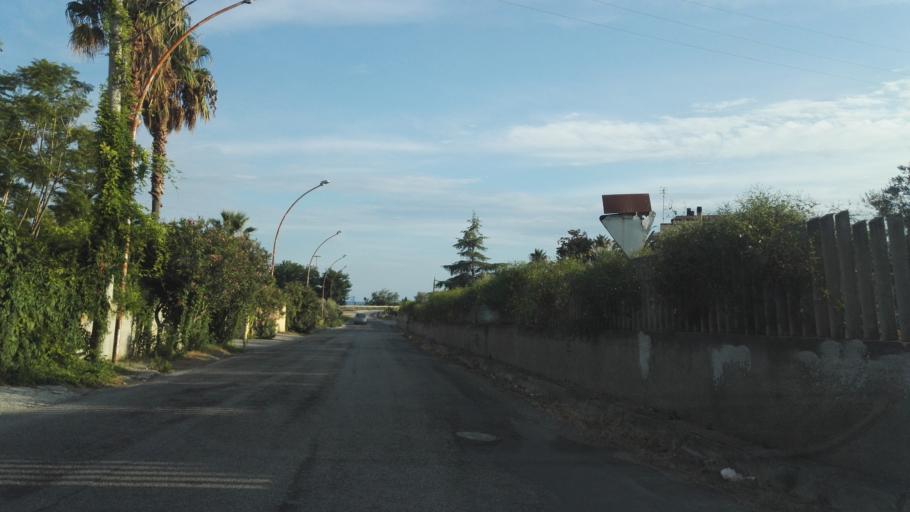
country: IT
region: Calabria
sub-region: Provincia di Reggio Calabria
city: Caulonia Marina
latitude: 38.3587
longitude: 16.4855
